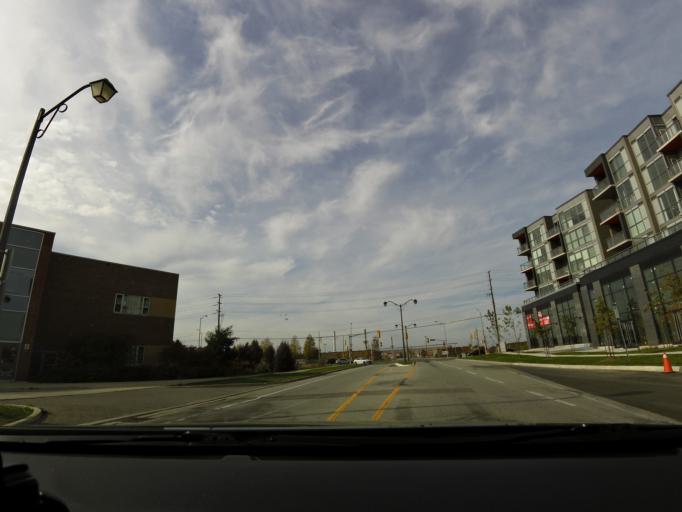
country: CA
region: Ontario
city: Burlington
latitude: 43.4115
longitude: -79.8011
